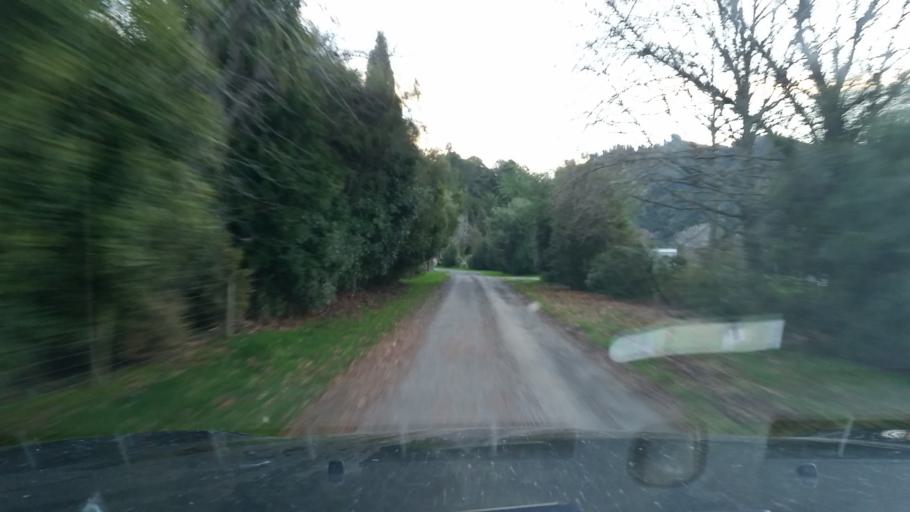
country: NZ
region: Marlborough
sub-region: Marlborough District
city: Blenheim
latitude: -41.4731
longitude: 173.7429
